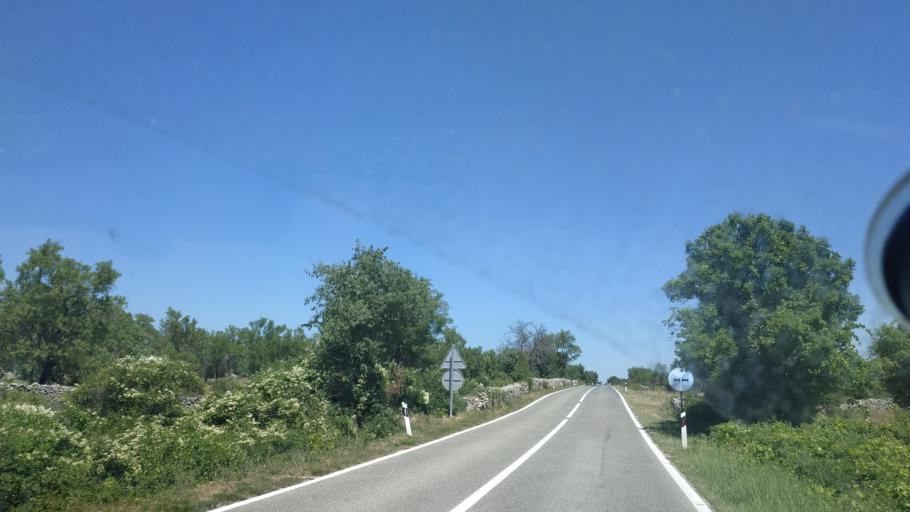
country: HR
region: Sibensko-Kniniska
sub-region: Grad Sibenik
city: Sibenik
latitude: 43.7897
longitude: 16.0260
